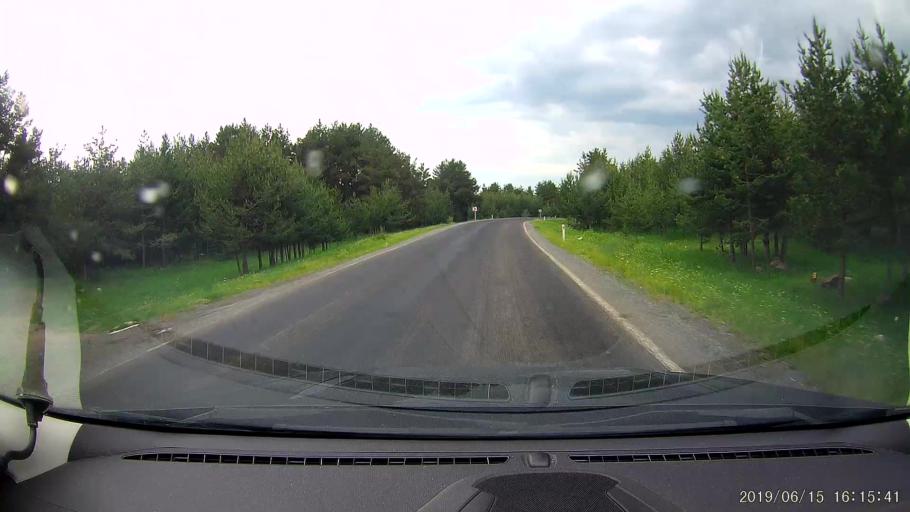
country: TR
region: Ardahan
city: Hanak
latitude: 41.2654
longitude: 42.8565
